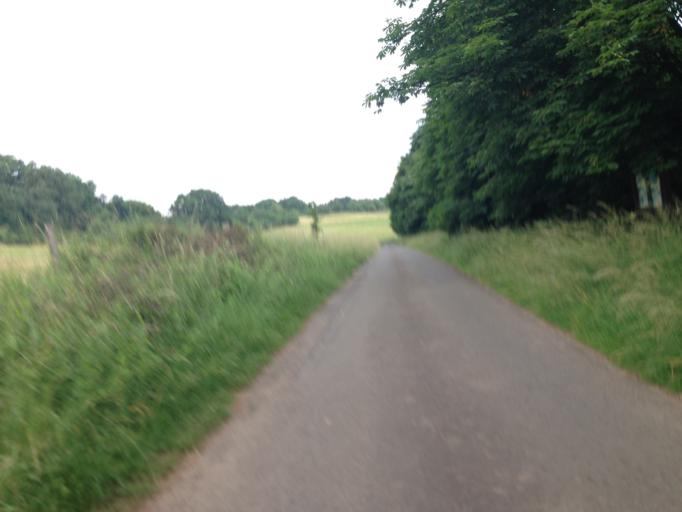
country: DE
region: Hesse
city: Wetter
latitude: 50.8569
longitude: 8.7321
